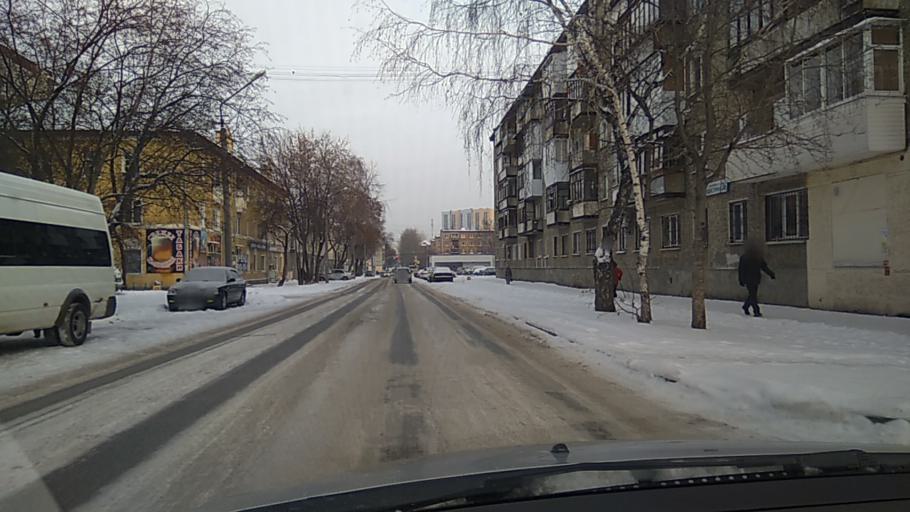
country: RU
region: Sverdlovsk
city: Yekaterinburg
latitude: 56.8976
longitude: 60.5965
